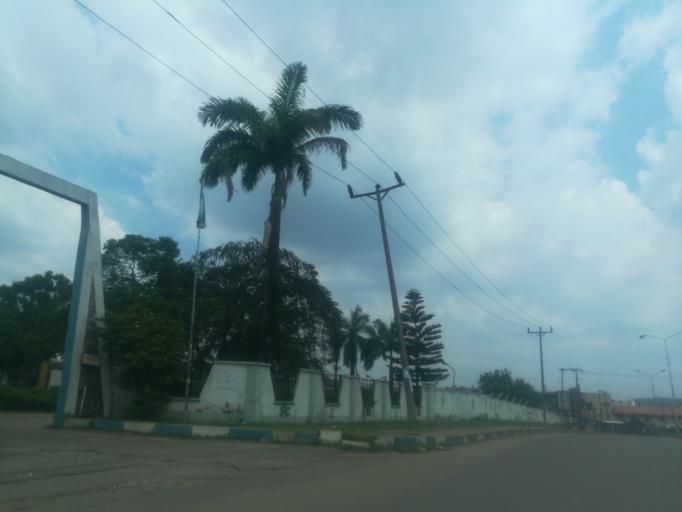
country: NG
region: Oyo
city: Ibadan
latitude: 7.3993
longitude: 3.8847
